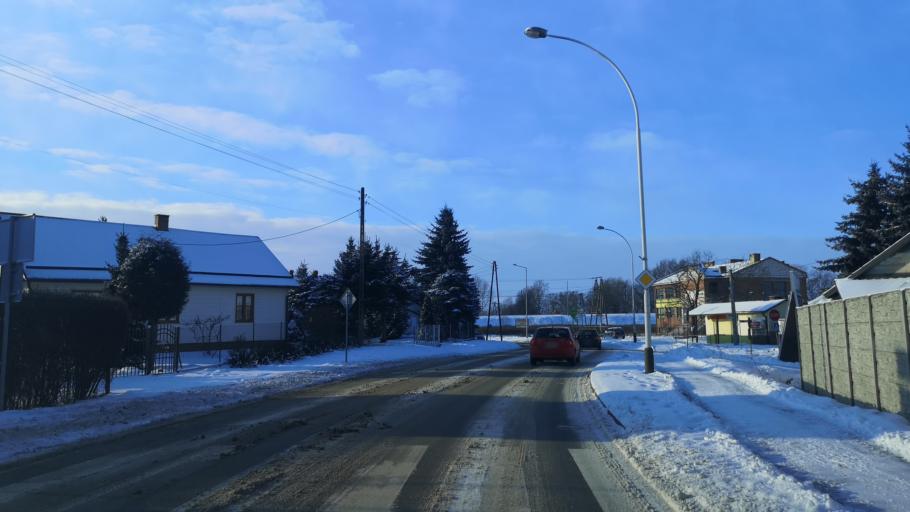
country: PL
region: Subcarpathian Voivodeship
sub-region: Powiat przeworski
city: Przeworsk
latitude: 50.0731
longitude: 22.4923
